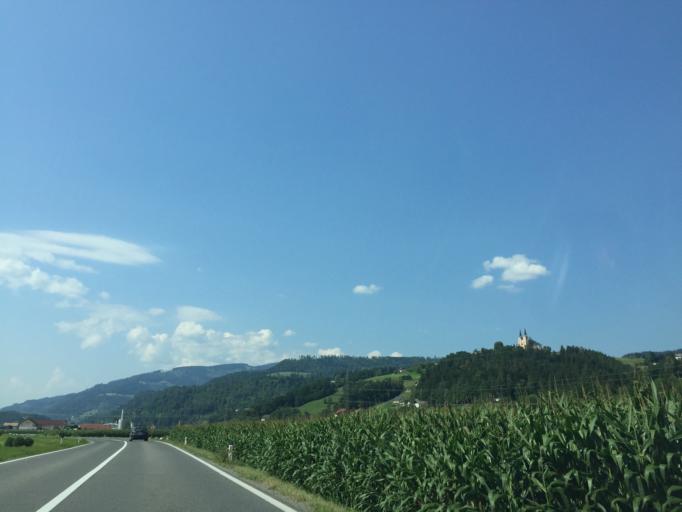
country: SI
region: Dravograd
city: Dravograd
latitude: 46.5566
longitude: 15.0436
